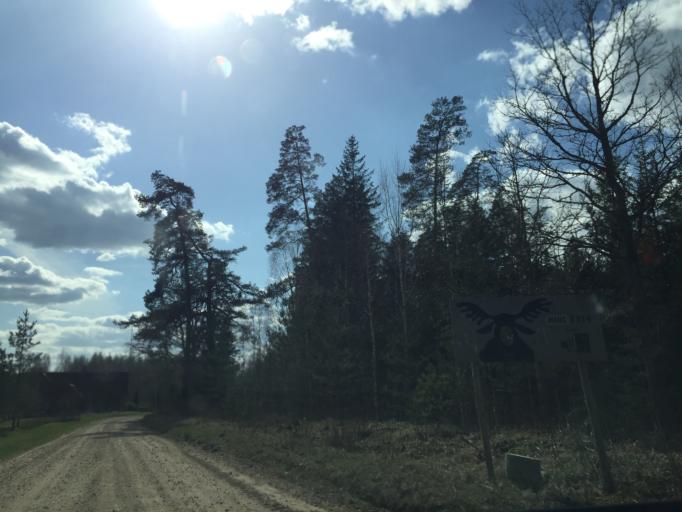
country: LV
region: Skriveri
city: Skriveri
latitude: 56.7847
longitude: 25.2356
